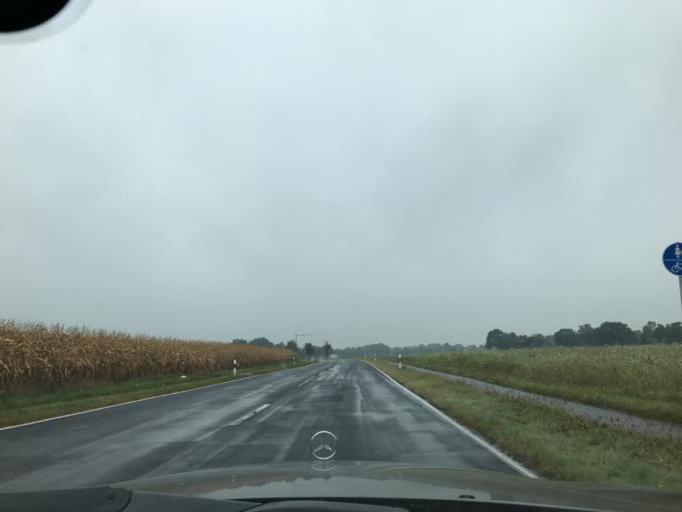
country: DE
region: Lower Saxony
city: Papenburg
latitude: 53.0768
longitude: 7.3487
